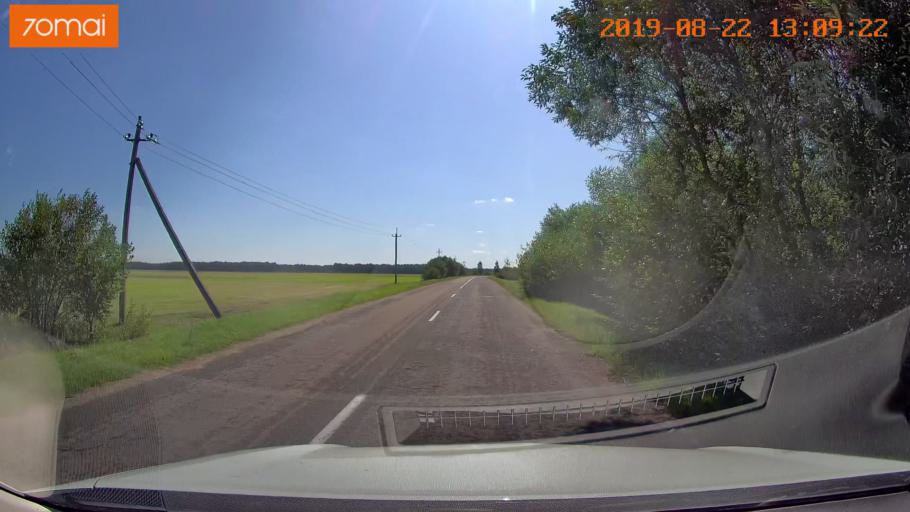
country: BY
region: Minsk
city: Prawdzinski
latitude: 53.3111
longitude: 27.8507
